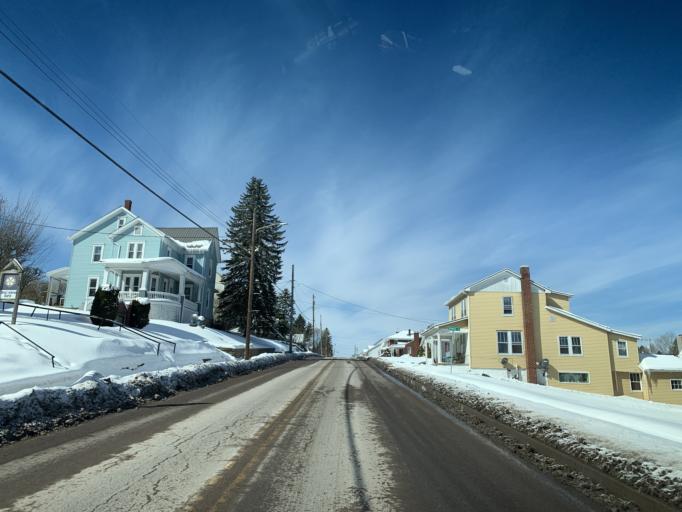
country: US
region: Pennsylvania
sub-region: Somerset County
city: Meyersdale
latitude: 39.6973
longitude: -79.1585
